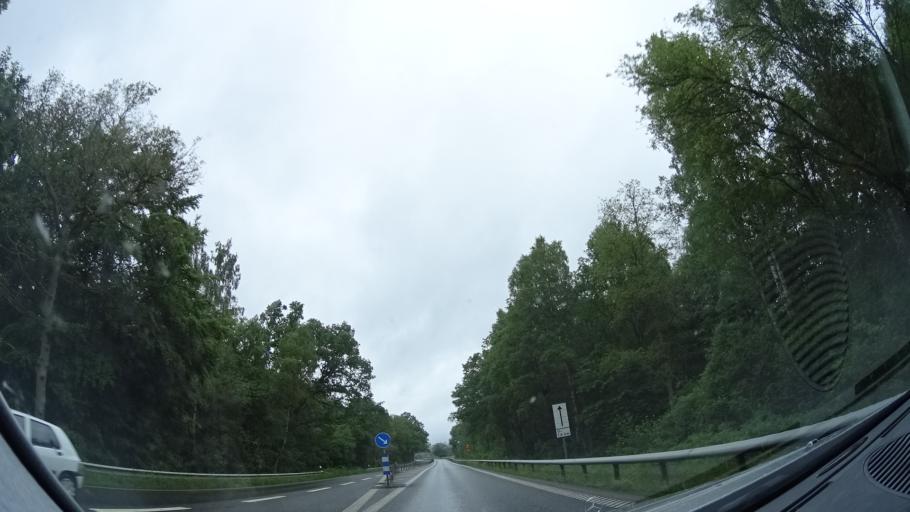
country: SE
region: Skane
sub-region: Hoors Kommun
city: Satofta
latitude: 55.8882
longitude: 13.5230
